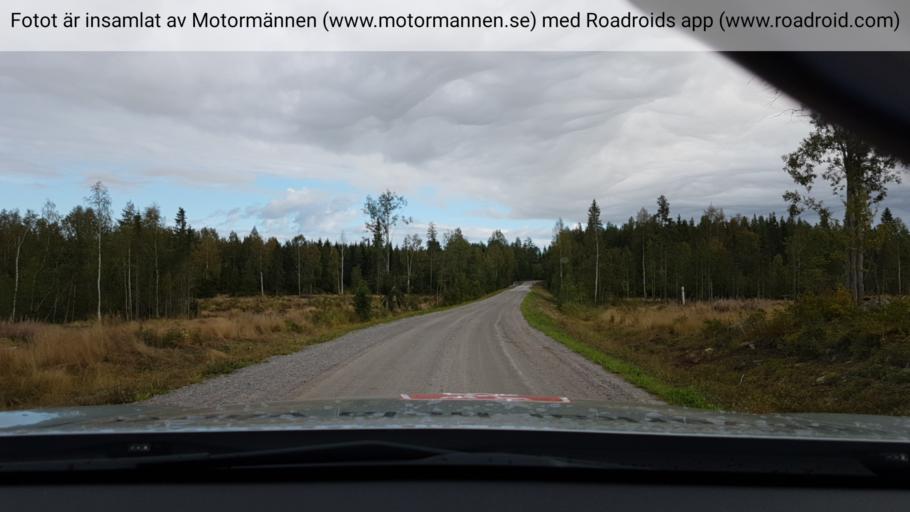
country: SE
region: Vaesterbotten
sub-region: Skelleftea Kommun
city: Byske
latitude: 65.1048
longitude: 21.1747
